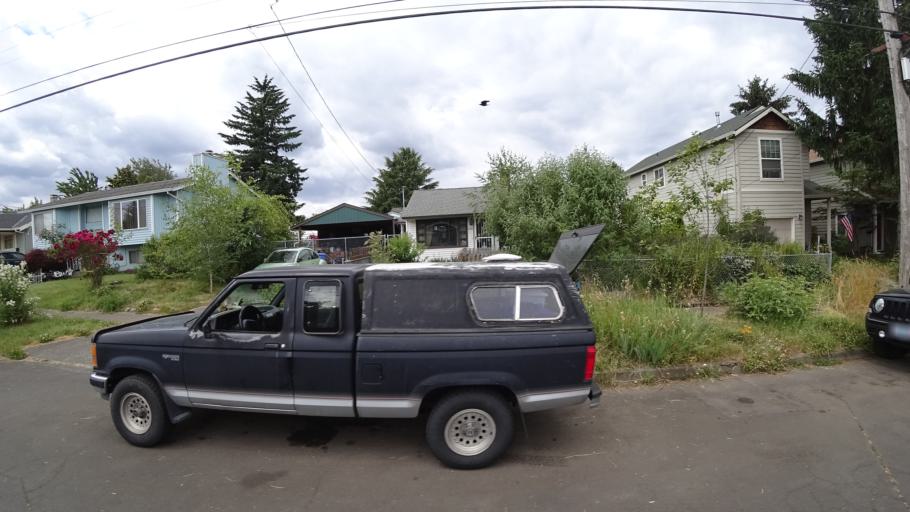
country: US
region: Washington
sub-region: Clark County
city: Vancouver
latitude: 45.5890
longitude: -122.7242
